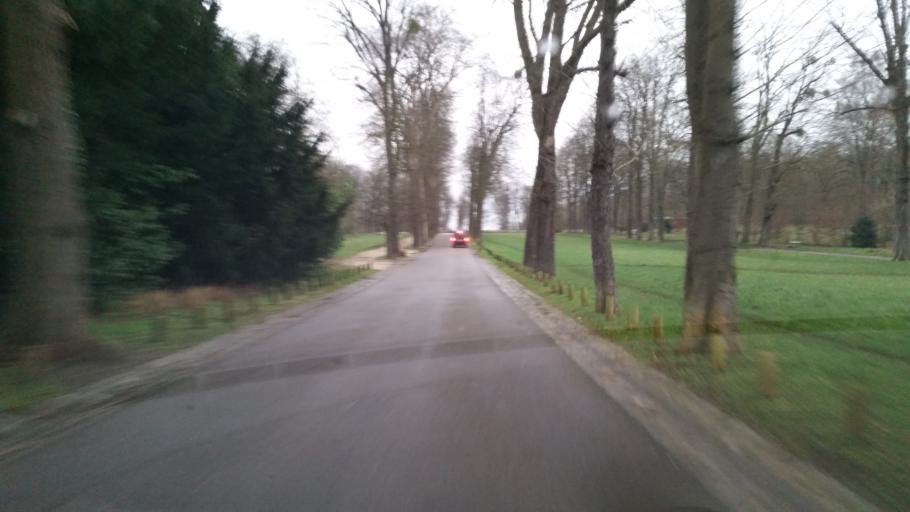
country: FR
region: Ile-de-France
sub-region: Departement des Hauts-de-Seine
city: Saint-Cloud
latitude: 48.8370
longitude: 2.2040
